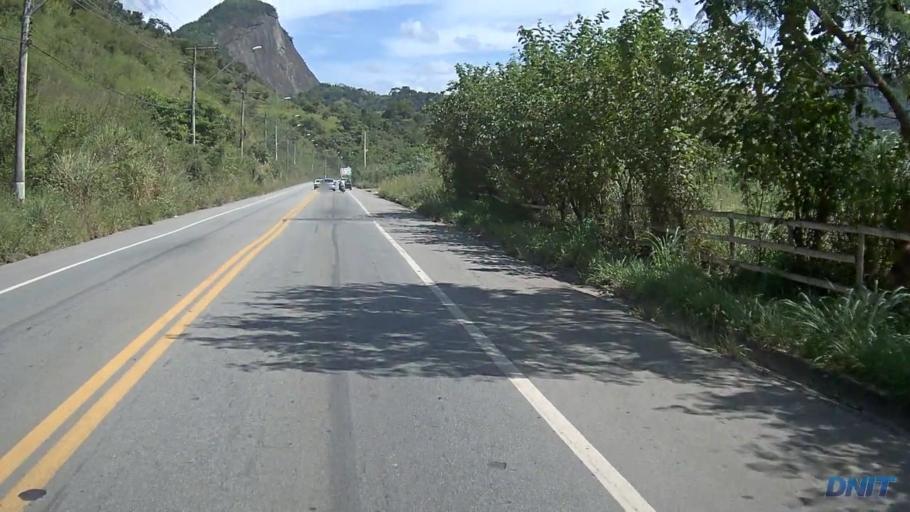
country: BR
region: Minas Gerais
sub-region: Timoteo
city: Timoteo
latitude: -19.5434
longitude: -42.6751
